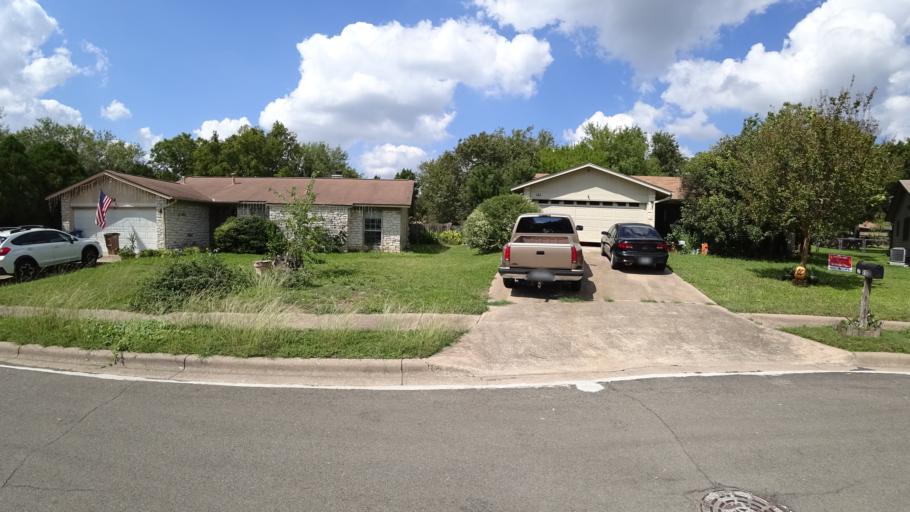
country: US
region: Texas
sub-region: Travis County
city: Onion Creek
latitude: 30.1909
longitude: -97.7861
